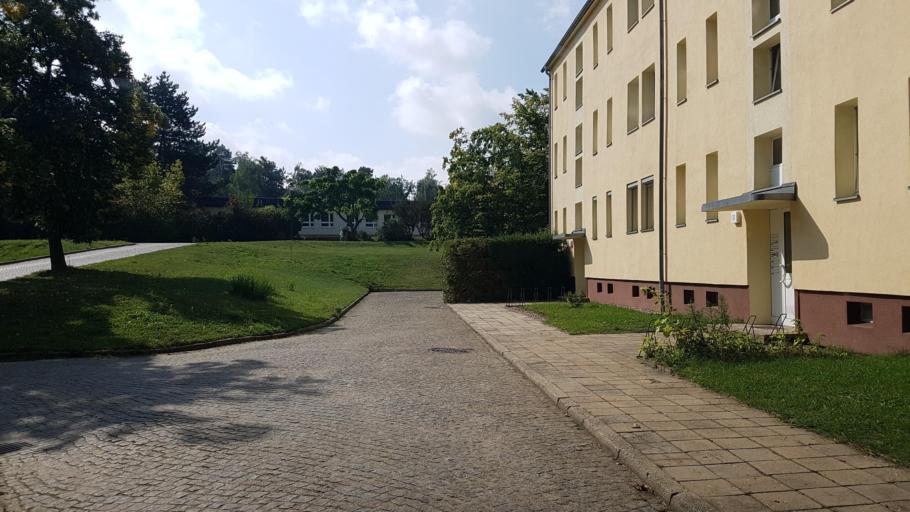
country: DE
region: Brandenburg
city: Luckau
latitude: 51.8555
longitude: 13.6975
